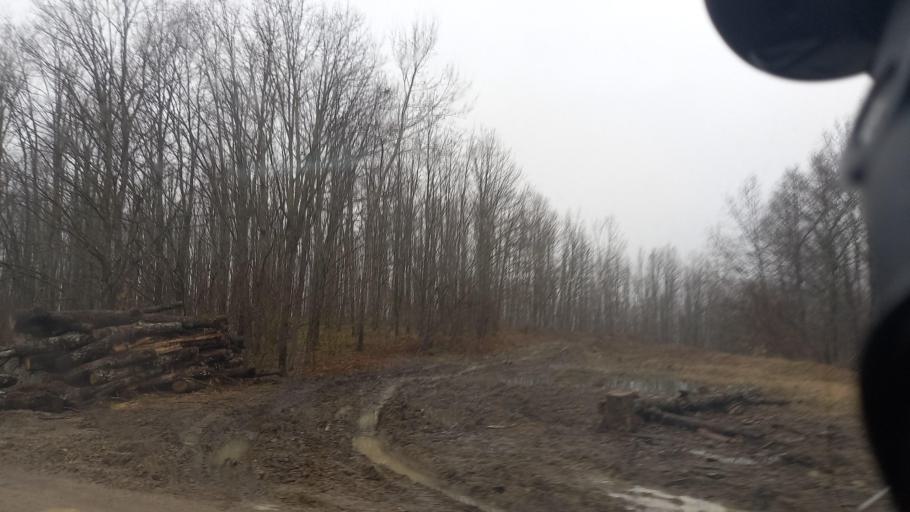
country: RU
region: Krasnodarskiy
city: Saratovskaya
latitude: 44.6154
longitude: 39.2475
